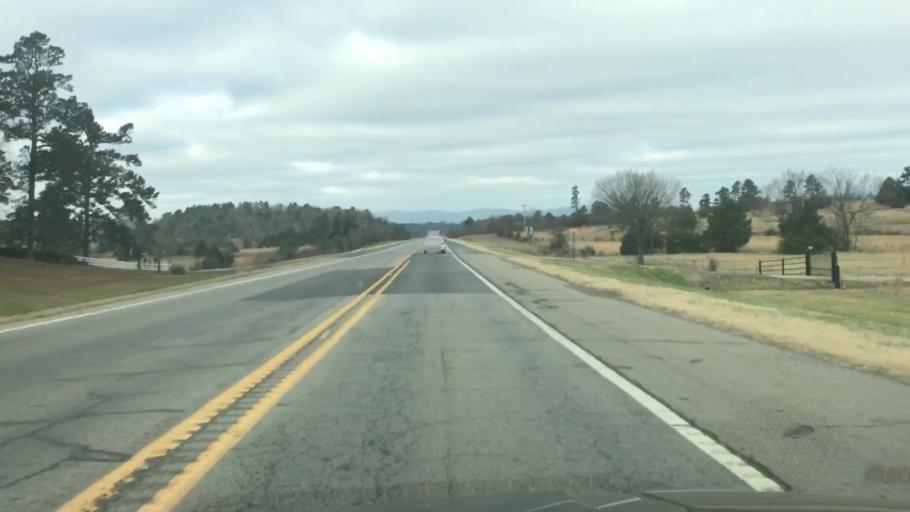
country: US
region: Arkansas
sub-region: Scott County
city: Waldron
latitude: 34.8692
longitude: -94.0809
